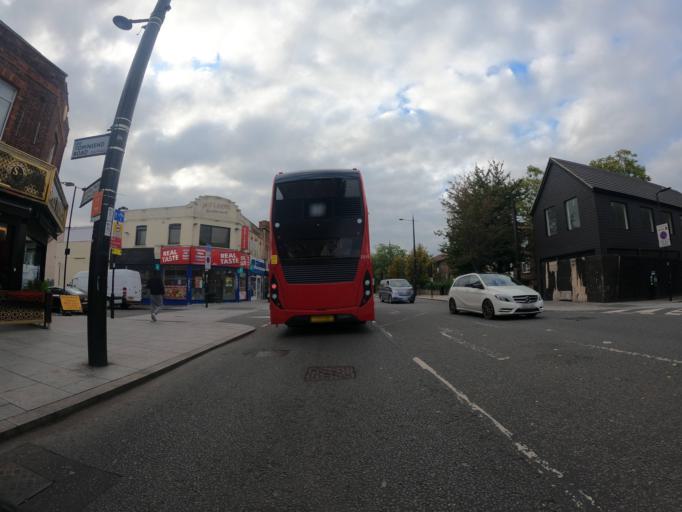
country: GB
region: England
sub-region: Greater London
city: Southall
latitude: 51.5124
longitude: -0.3849
